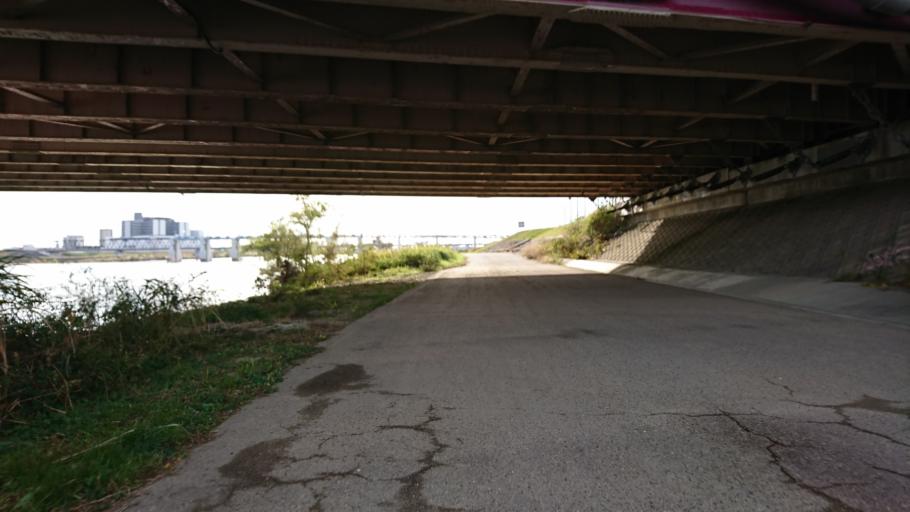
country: JP
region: Hyogo
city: Kakogawacho-honmachi
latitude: 34.7777
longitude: 134.8373
